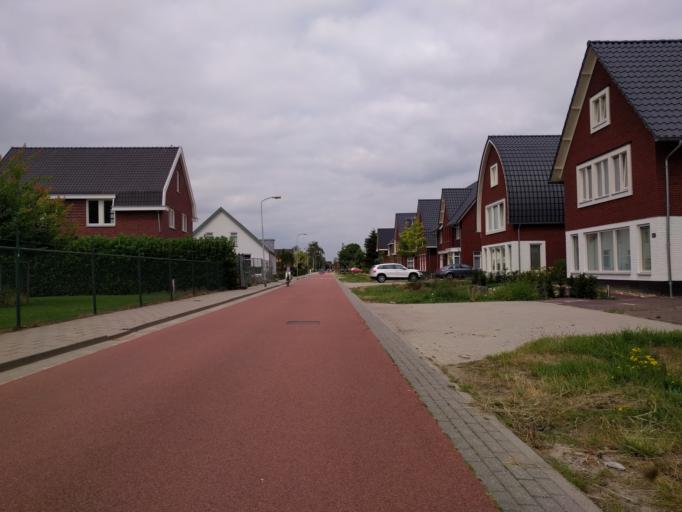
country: NL
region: Gelderland
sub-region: Gemeente Nijmegen
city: Nijmegen
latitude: 51.8654
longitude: 5.8681
